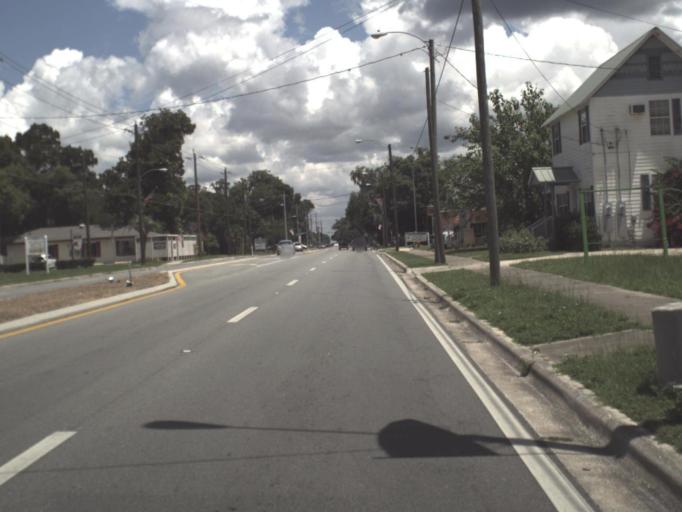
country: US
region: Florida
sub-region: Putnam County
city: Crescent City
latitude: 29.4331
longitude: -81.5104
